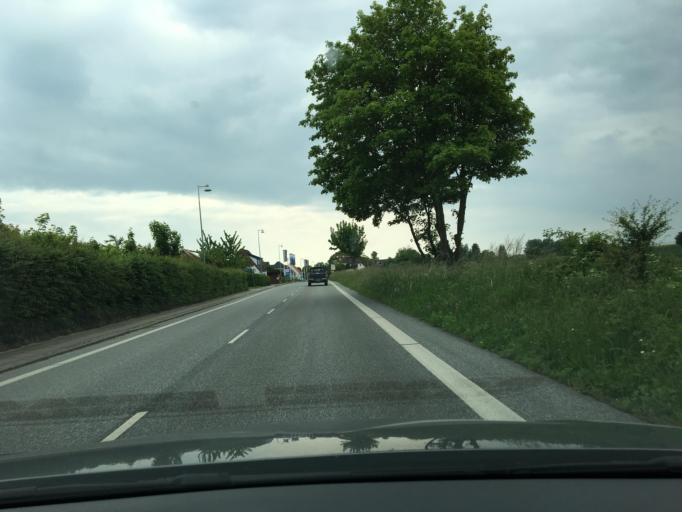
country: DK
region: South Denmark
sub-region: Assens Kommune
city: Assens
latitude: 55.2802
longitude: 9.9169
